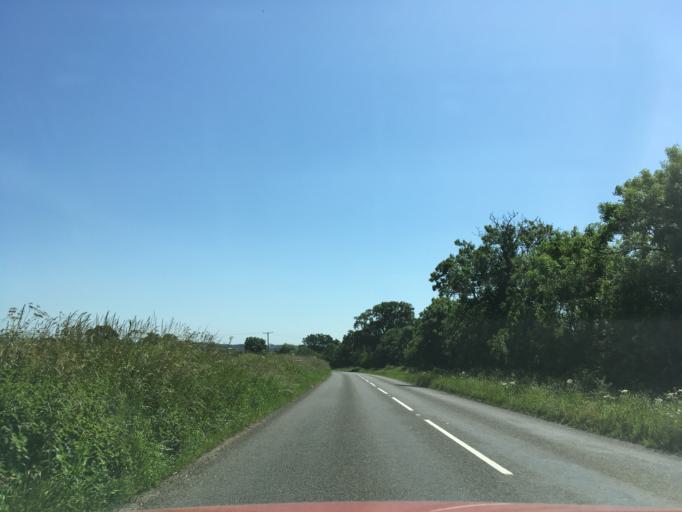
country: GB
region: England
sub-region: Oxfordshire
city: Deddington
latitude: 51.9818
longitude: -1.2982
